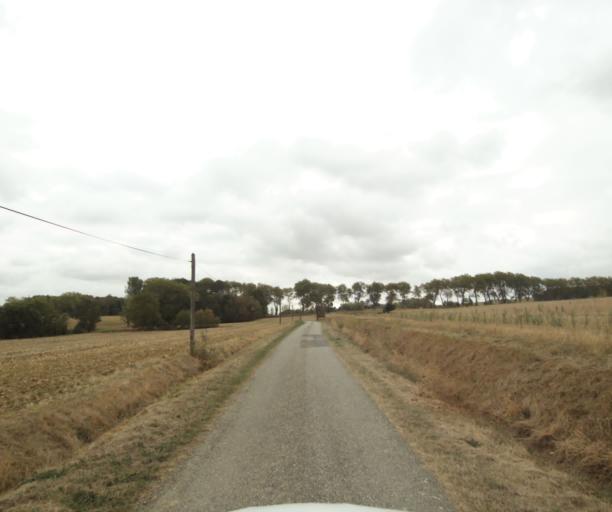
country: FR
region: Midi-Pyrenees
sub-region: Departement de la Haute-Garonne
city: Villefranche-de-Lauragais
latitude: 43.4160
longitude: 1.7374
